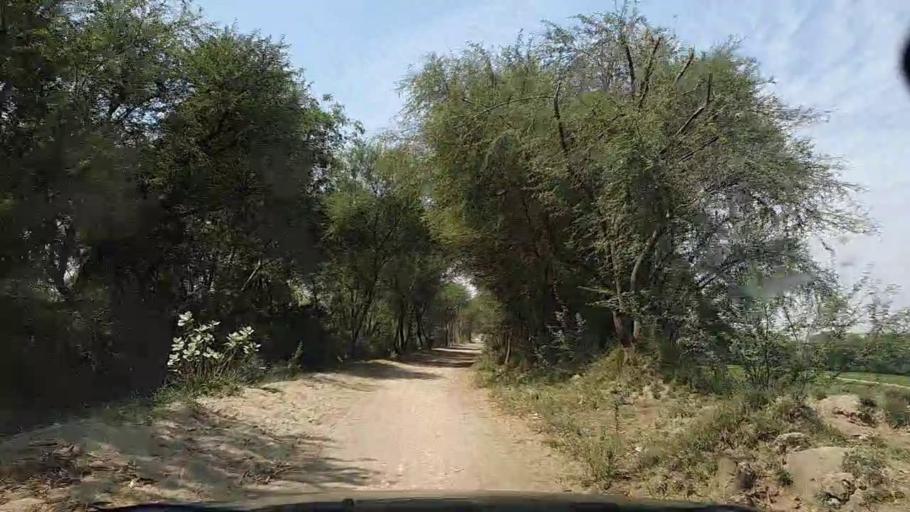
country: PK
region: Sindh
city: Mirpur Batoro
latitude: 24.6491
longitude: 68.1555
